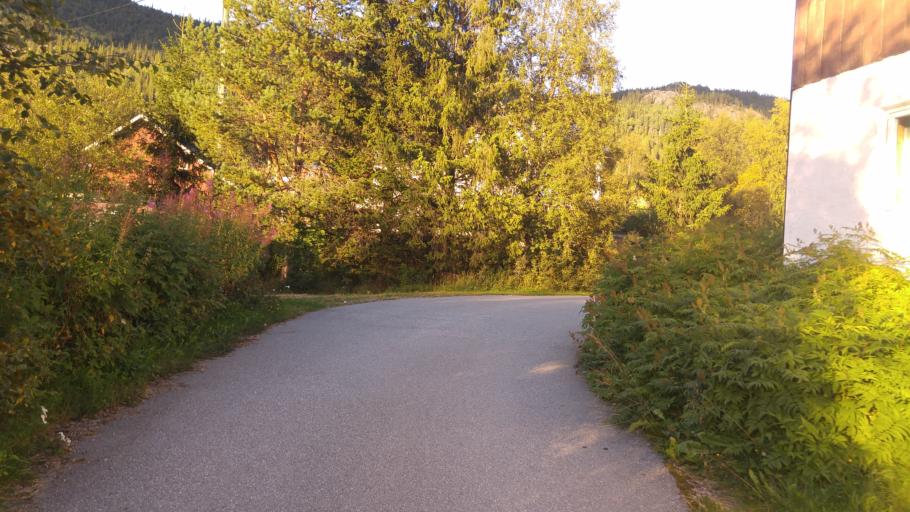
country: NO
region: Buskerud
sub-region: Hemsedal
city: Troim
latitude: 60.8509
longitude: 8.6145
